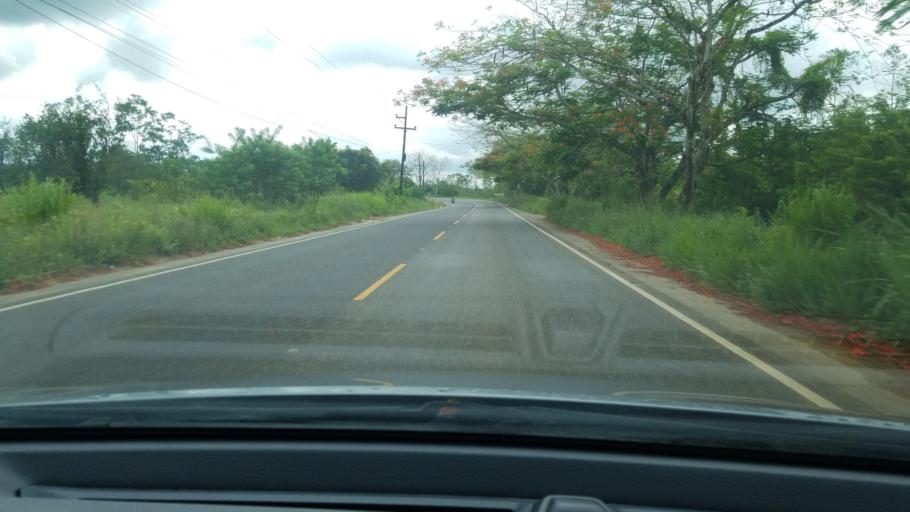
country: HN
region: Cortes
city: Potrerillos
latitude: 15.5958
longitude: -88.3166
